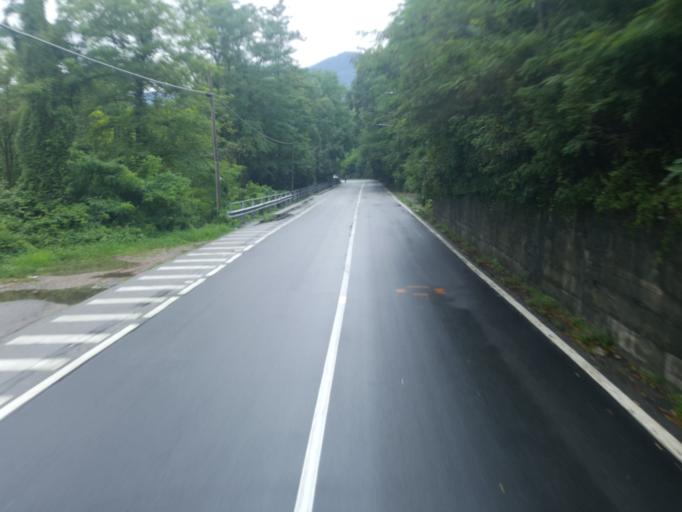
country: IT
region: Piedmont
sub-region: Provincia Verbano-Cusio-Ossola
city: Pallanza-Intra-Suna
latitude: 45.9453
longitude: 8.5659
